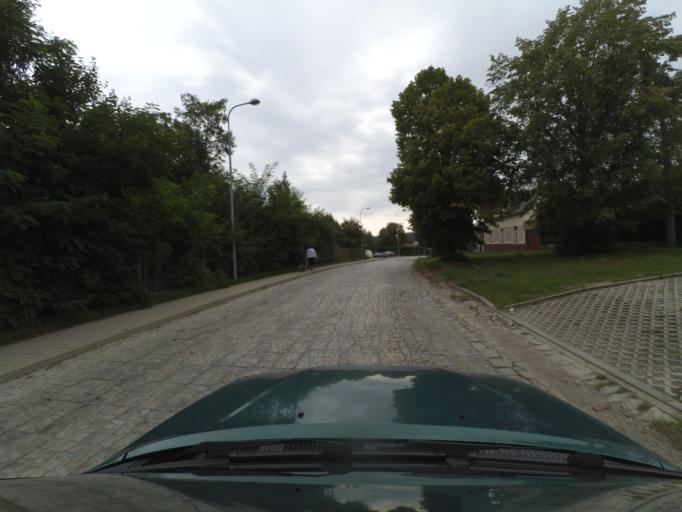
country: CZ
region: Plzensky
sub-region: Okres Plzen-Sever
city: Tremosna
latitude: 49.8175
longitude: 13.3906
